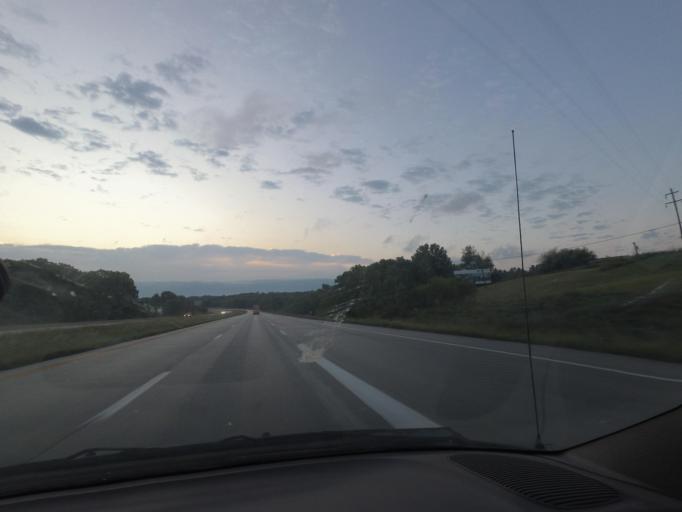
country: US
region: Missouri
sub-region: Macon County
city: Macon
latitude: 39.7478
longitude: -92.5010
